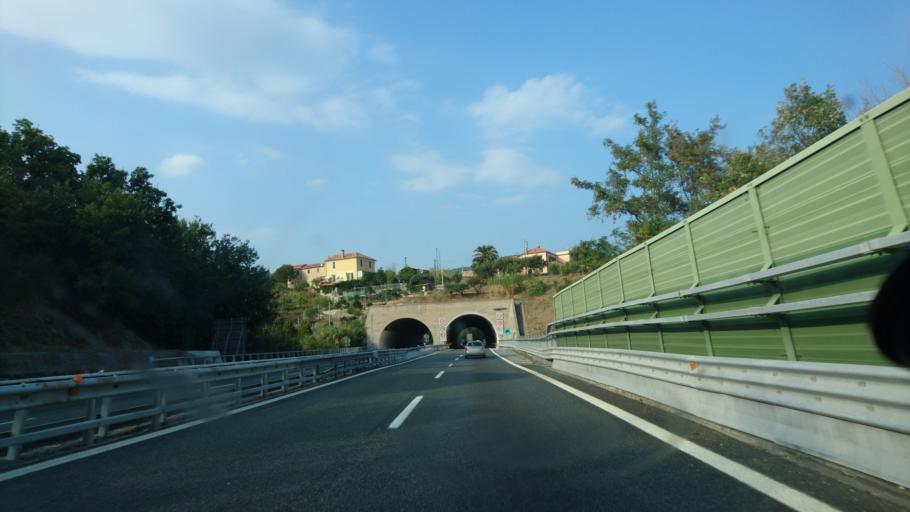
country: IT
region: Liguria
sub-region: Provincia di Savona
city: Valleggia
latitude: 44.2965
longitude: 8.4464
